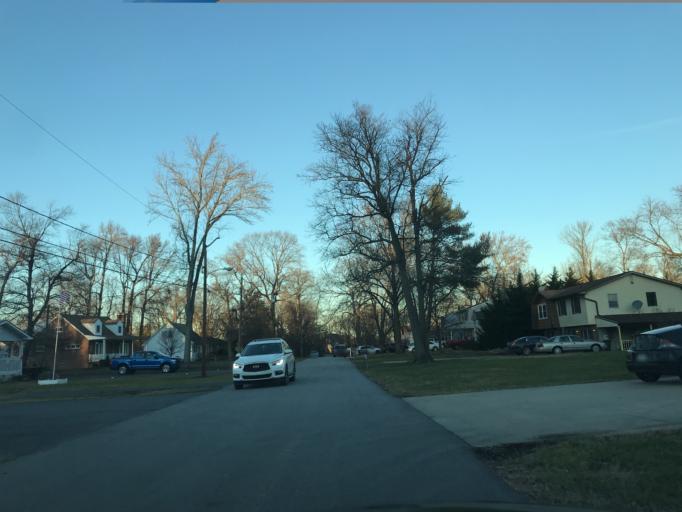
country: US
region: Maryland
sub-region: Baltimore County
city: Bowleys Quarters
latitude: 39.3738
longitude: -76.3543
